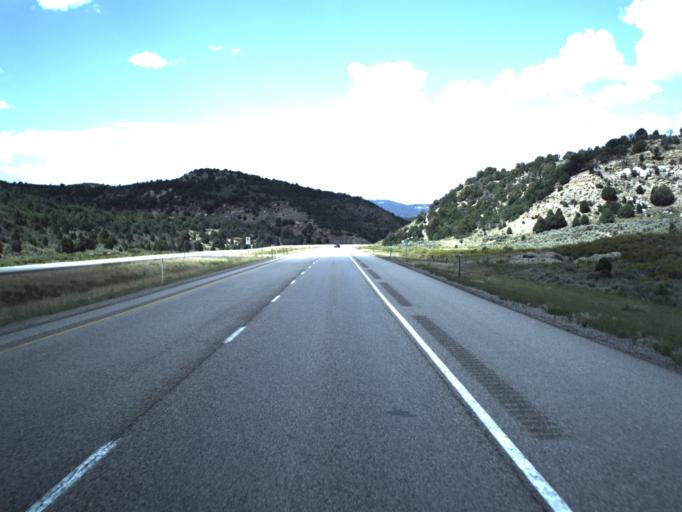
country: US
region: Utah
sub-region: Sevier County
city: Salina
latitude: 38.7857
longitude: -111.4978
